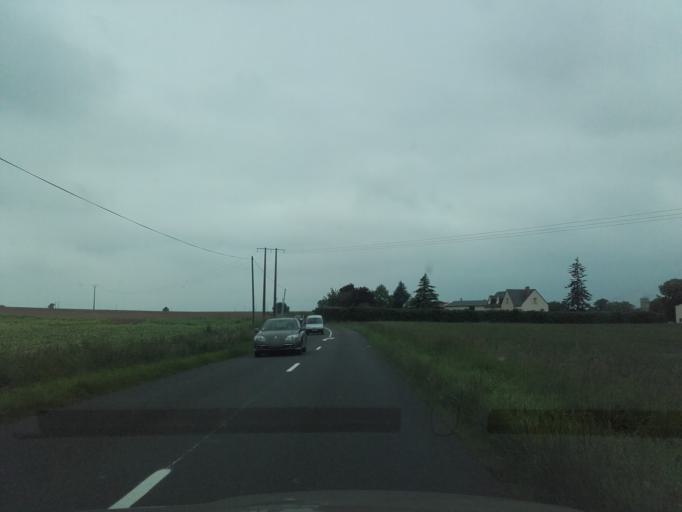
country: FR
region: Centre
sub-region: Departement du Loir-et-Cher
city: Savigny-sur-Braye
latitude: 47.8946
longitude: 0.7780
